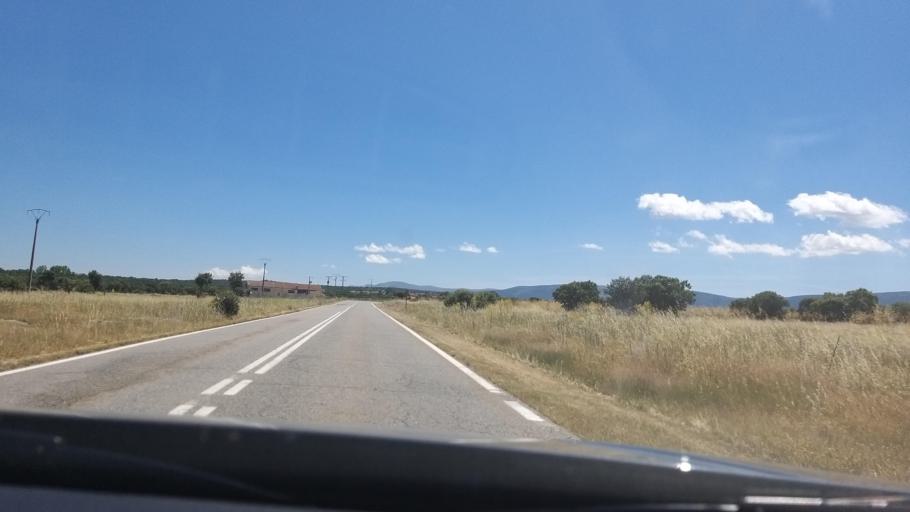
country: ES
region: Castille and Leon
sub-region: Provincia de Segovia
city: Pedraza
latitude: 41.1298
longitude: -3.7912
